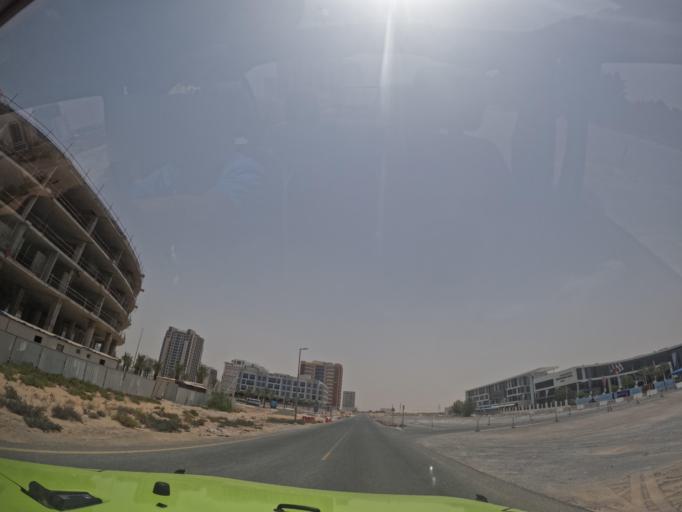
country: AE
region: Dubai
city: Dubai
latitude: 25.0907
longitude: 55.3759
